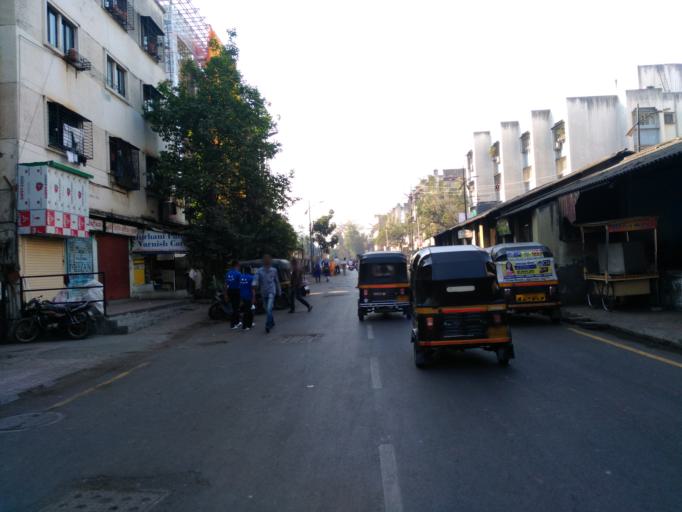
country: IN
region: Maharashtra
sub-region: Pune Division
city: Pune
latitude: 18.5092
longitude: 73.8724
